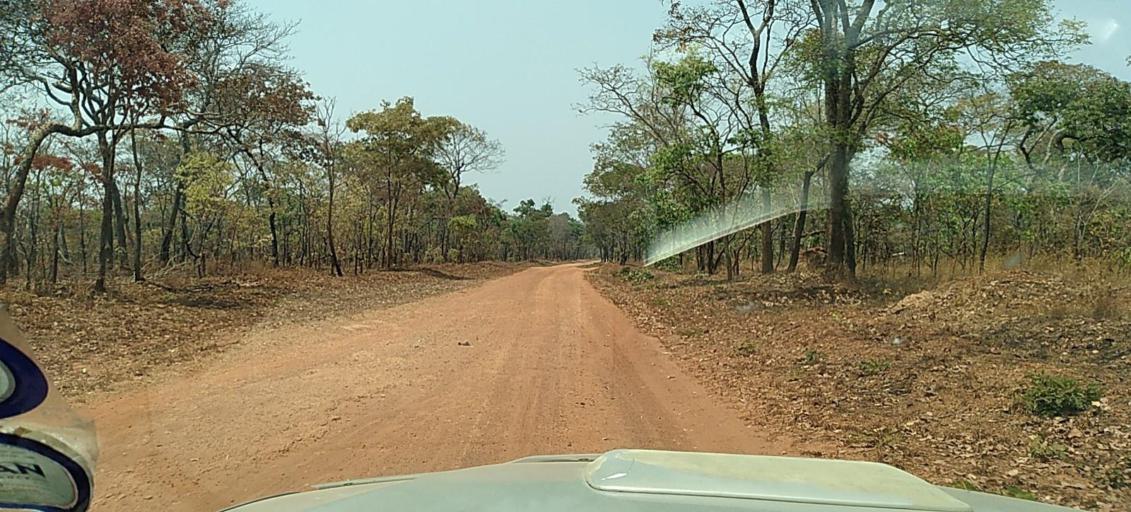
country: ZM
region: North-Western
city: Kasempa
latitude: -13.5636
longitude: 26.0893
